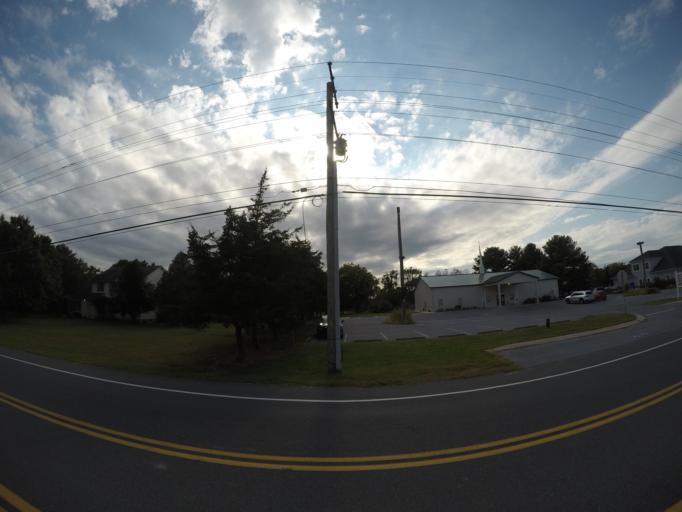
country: US
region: Delaware
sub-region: Sussex County
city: Lewes
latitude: 38.7273
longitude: -75.1468
